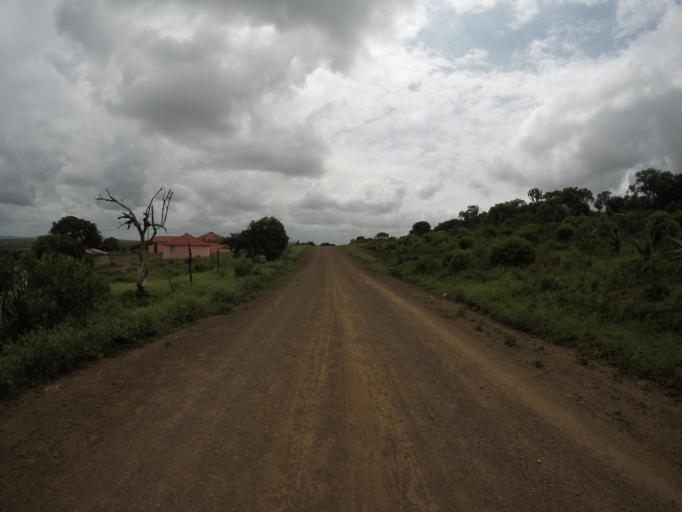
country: ZA
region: KwaZulu-Natal
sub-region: uThungulu District Municipality
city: Empangeni
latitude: -28.5795
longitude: 31.8675
